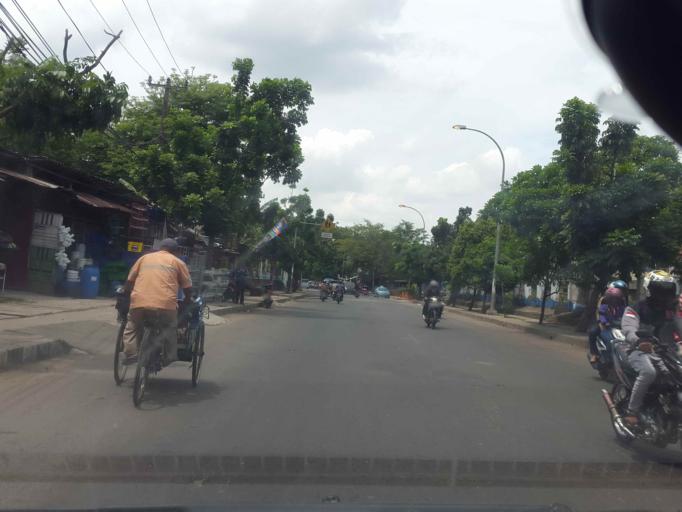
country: ID
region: Banten
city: Tangerang
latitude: -6.1706
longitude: 106.6154
